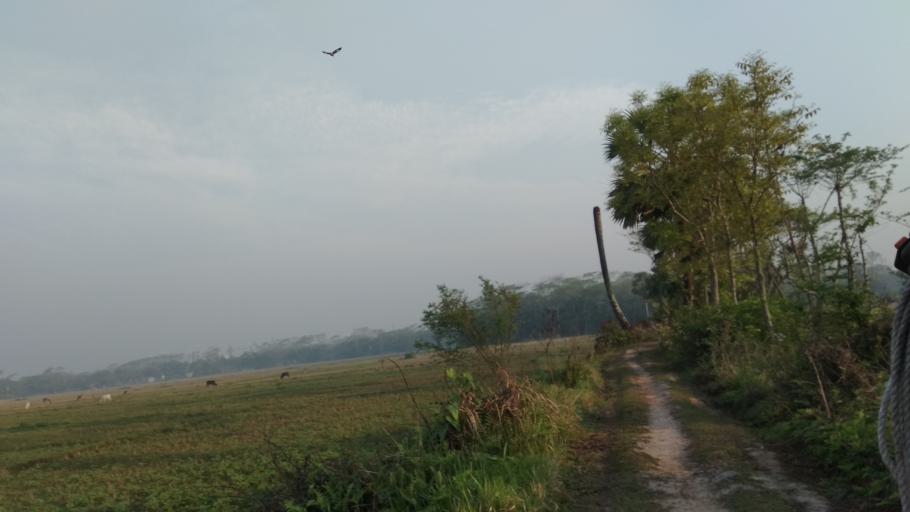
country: BD
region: Barisal
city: Mehendiganj
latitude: 22.9342
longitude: 90.4136
